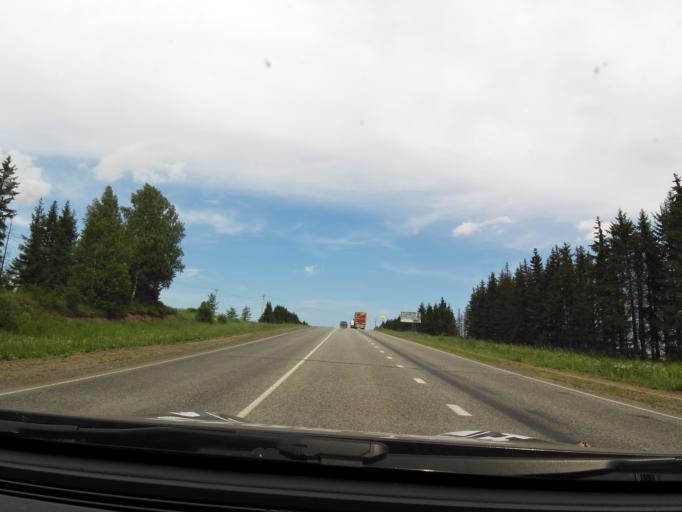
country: RU
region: Kirov
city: Stulovo
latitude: 58.7118
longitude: 50.1132
